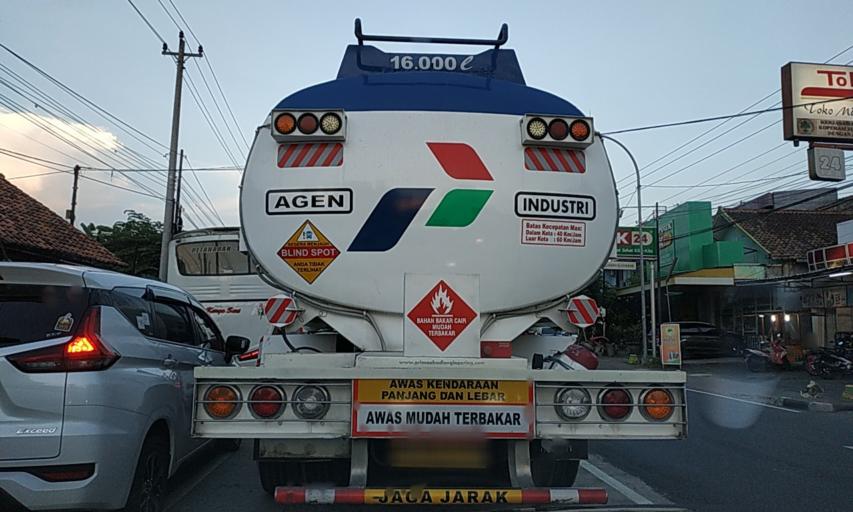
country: ID
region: Daerah Istimewa Yogyakarta
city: Srandakan
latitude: -7.8654
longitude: 110.1560
